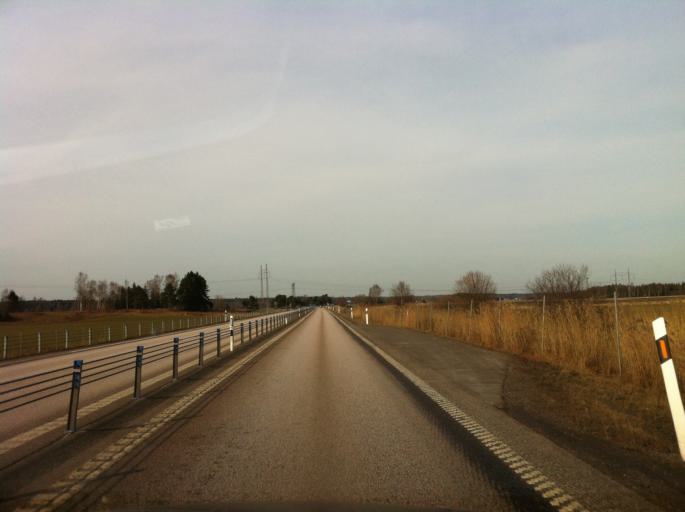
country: SE
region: Vaestra Goetaland
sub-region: Skovde Kommun
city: Stopen
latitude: 58.5593
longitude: 13.8040
